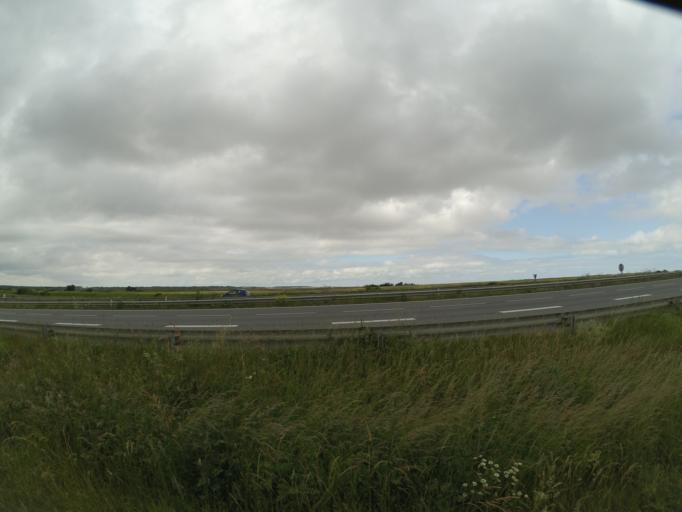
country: FR
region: Poitou-Charentes
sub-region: Departement de la Charente-Maritime
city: Yves
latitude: 46.0127
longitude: -1.0488
